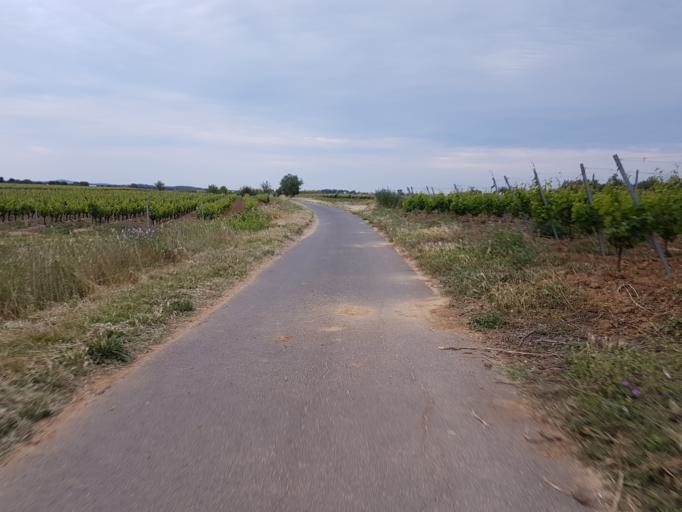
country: FR
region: Languedoc-Roussillon
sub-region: Departement de l'Herault
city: Cers
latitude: 43.3199
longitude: 3.3177
